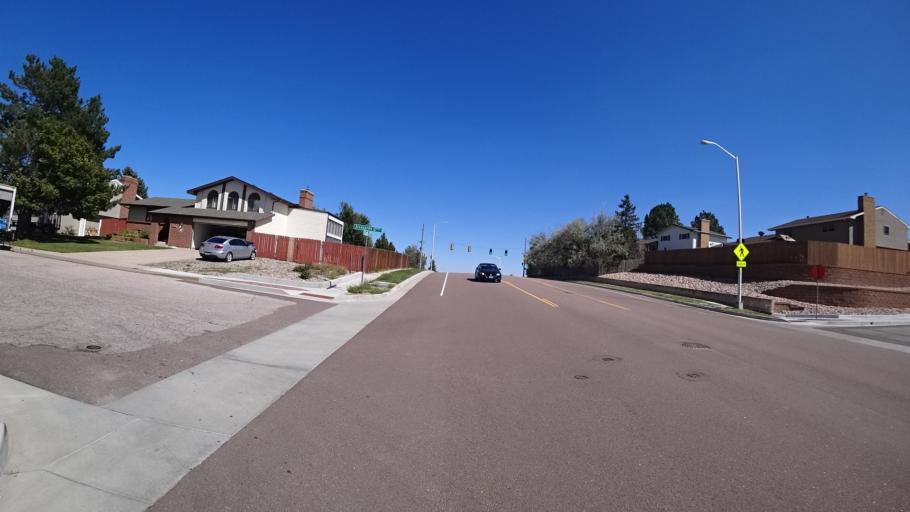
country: US
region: Colorado
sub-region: El Paso County
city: Cimarron Hills
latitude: 38.8769
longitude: -104.7290
